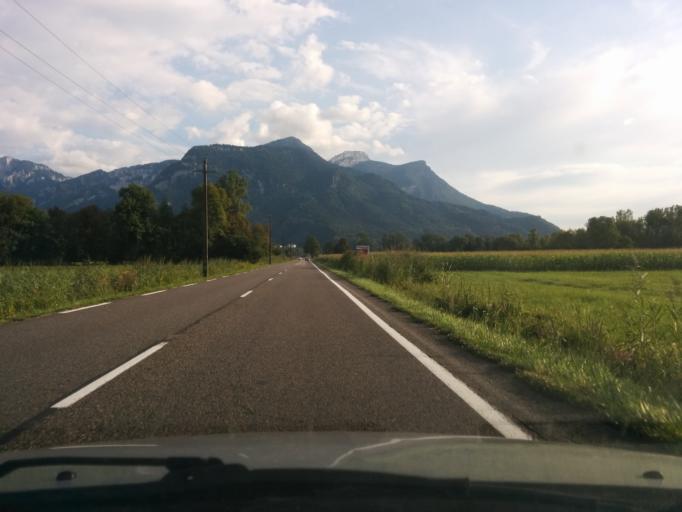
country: FR
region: Rhone-Alpes
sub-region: Departement de l'Isere
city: Saint-Laurent-du-Pont
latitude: 45.4080
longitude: 5.7470
